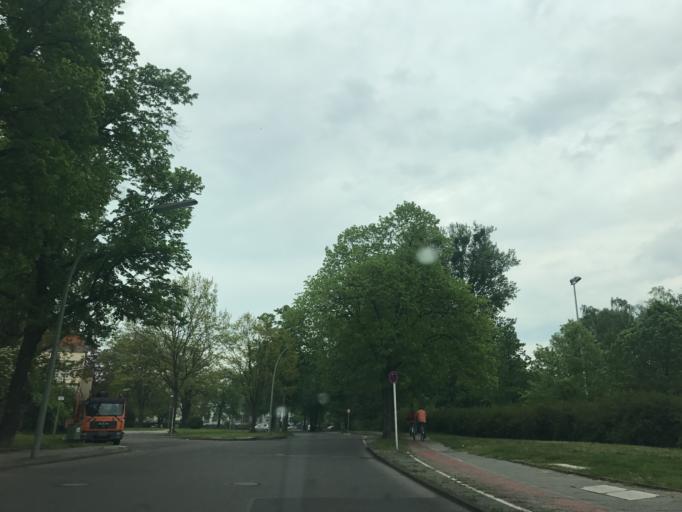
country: DE
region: Berlin
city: Spandau
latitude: 52.5537
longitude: 13.1942
